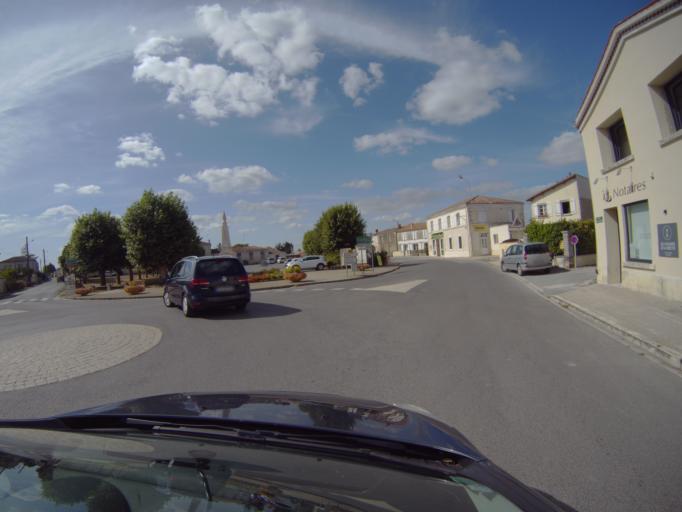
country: FR
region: Poitou-Charentes
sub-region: Departement des Deux-Sevres
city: Saint-Hilaire-la-Palud
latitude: 46.2638
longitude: -0.7130
